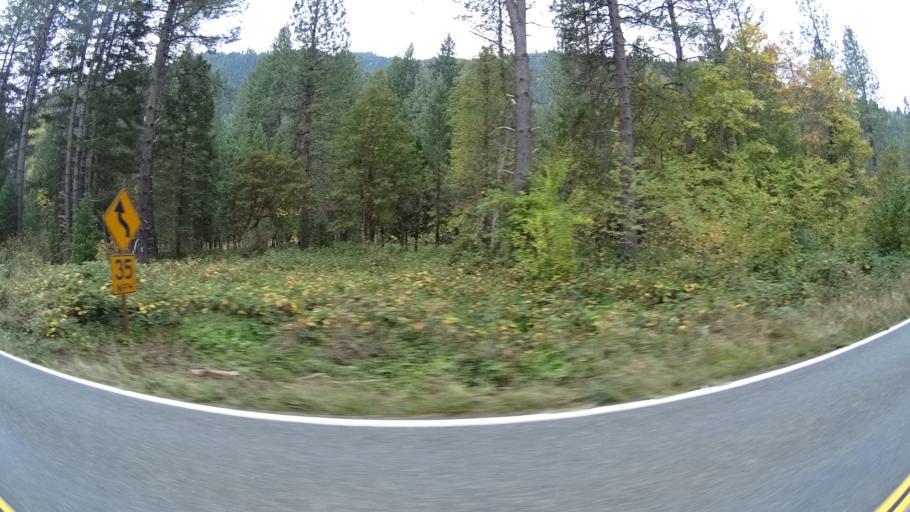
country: US
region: California
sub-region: Siskiyou County
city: Happy Camp
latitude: 41.8770
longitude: -123.4179
